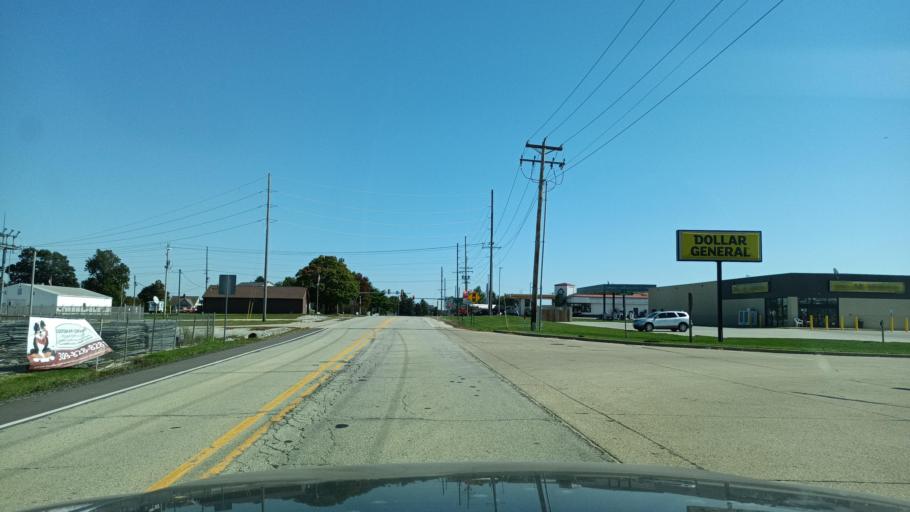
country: US
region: Illinois
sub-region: Woodford County
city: Eureka
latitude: 40.6277
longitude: -89.2775
